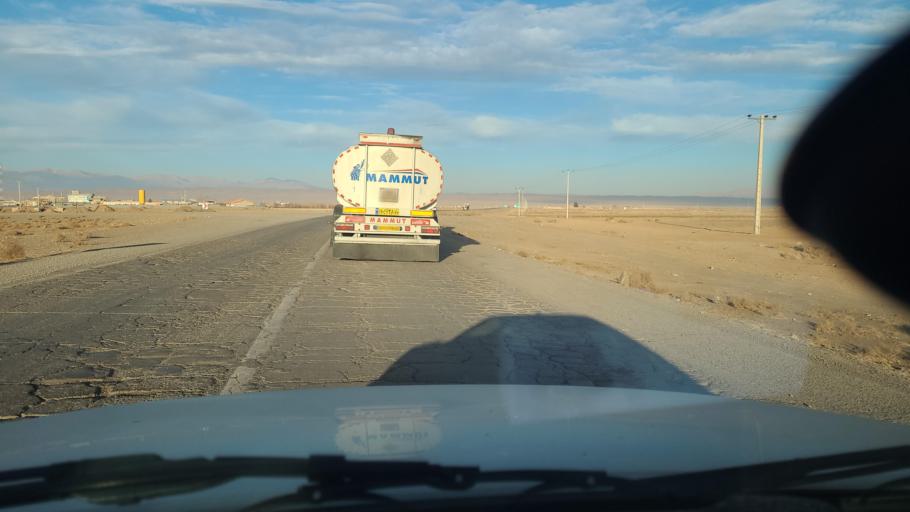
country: IR
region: Razavi Khorasan
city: Neqab
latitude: 36.6126
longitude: 57.5951
